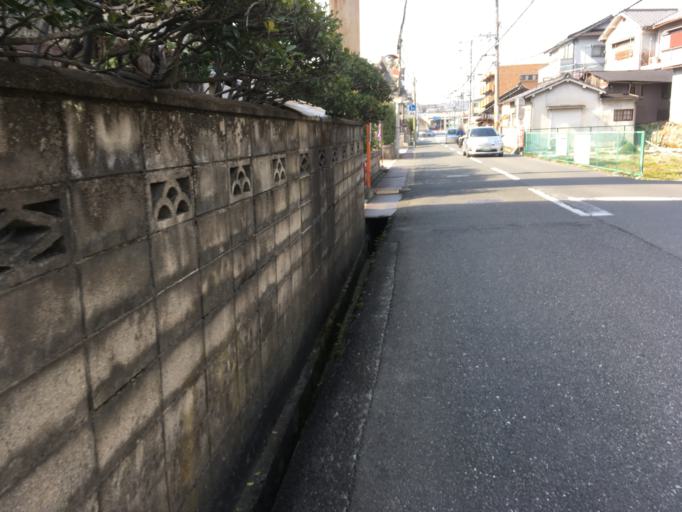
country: JP
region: Nara
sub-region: Ikoma-shi
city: Ikoma
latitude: 34.6905
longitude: 135.7048
